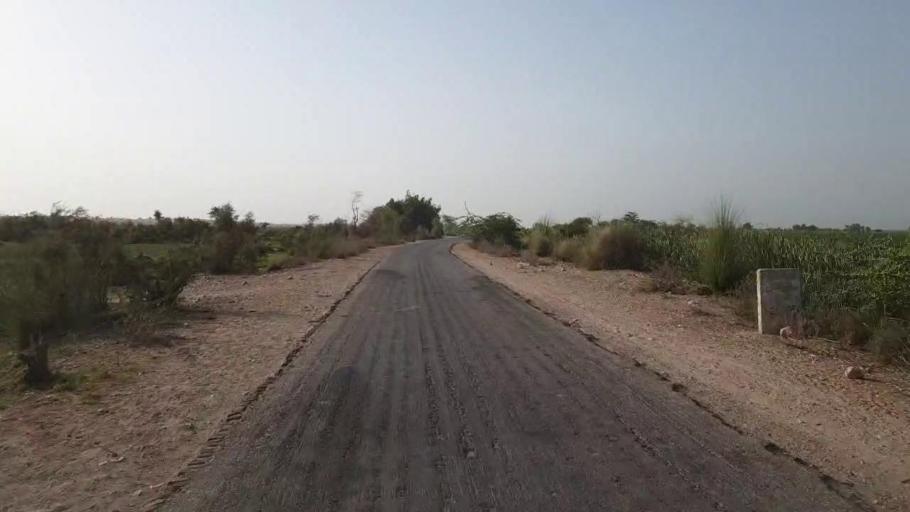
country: PK
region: Sindh
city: Jam Sahib
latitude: 26.4586
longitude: 68.8593
